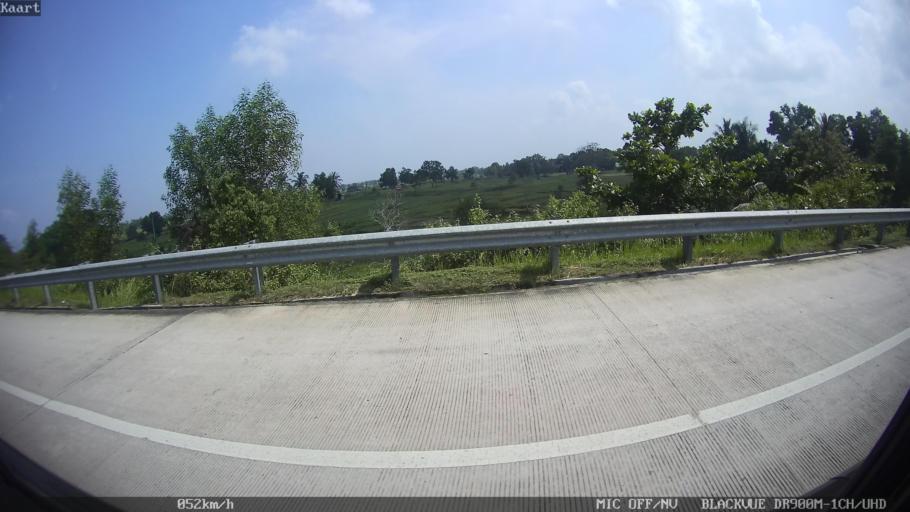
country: ID
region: Lampung
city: Natar
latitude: -5.2811
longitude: 105.1990
